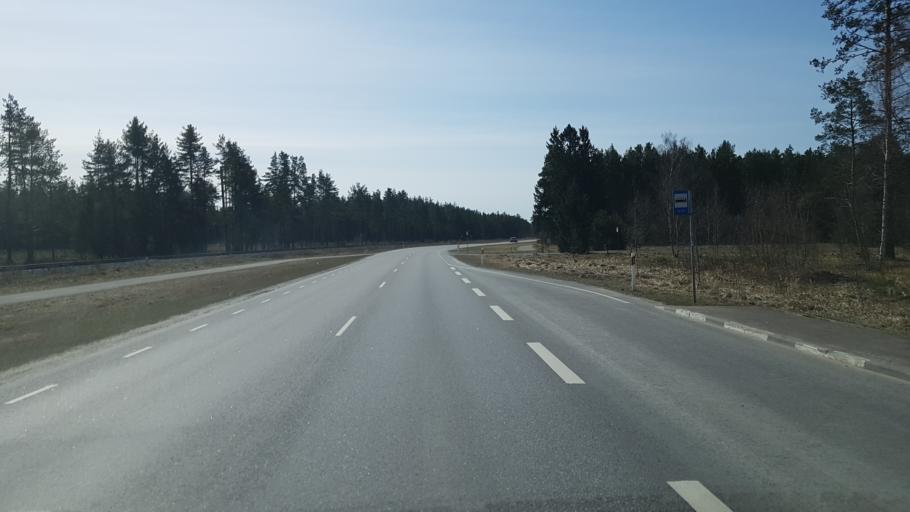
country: EE
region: Harju
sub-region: Saku vald
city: Saku
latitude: 59.2560
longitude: 24.6870
